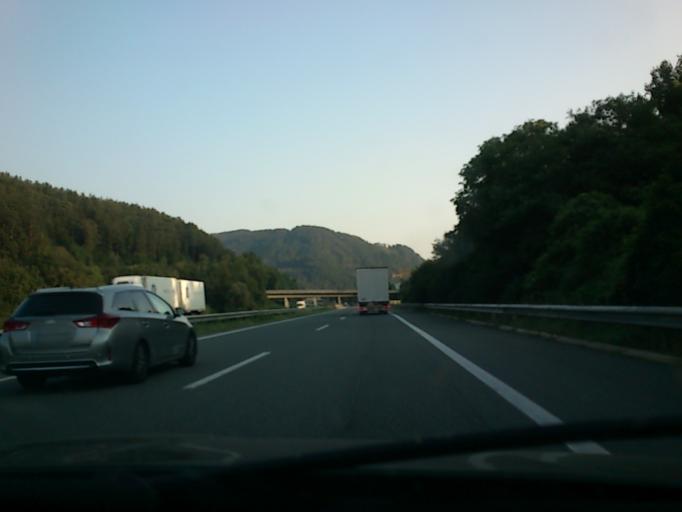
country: AT
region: Styria
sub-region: Politischer Bezirk Graz-Umgebung
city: Deutschfeistritz
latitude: 47.1824
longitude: 15.3310
